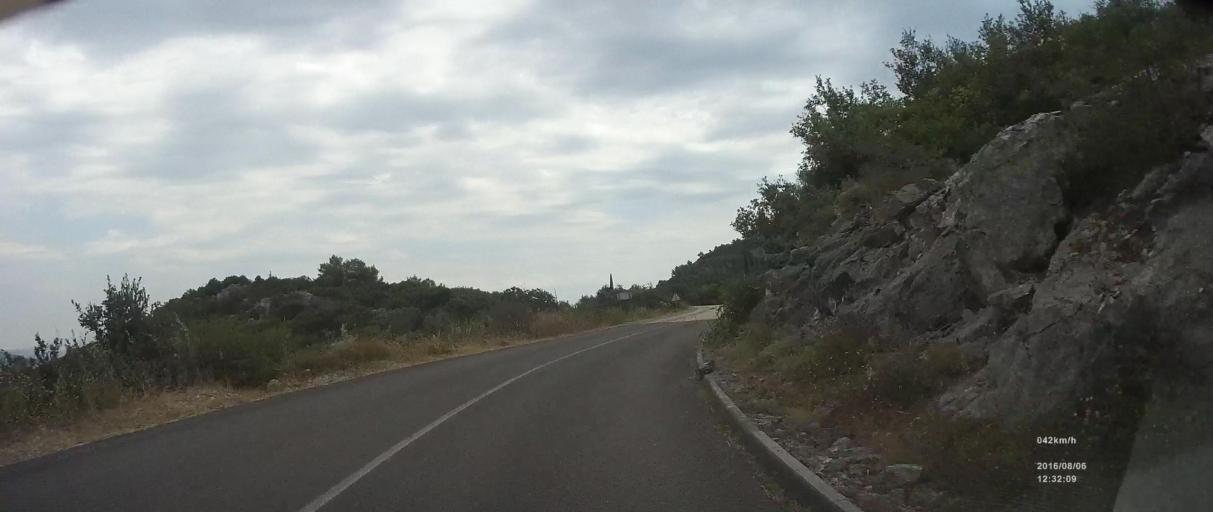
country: HR
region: Dubrovacko-Neretvanska
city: Ston
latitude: 42.7115
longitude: 17.7095
